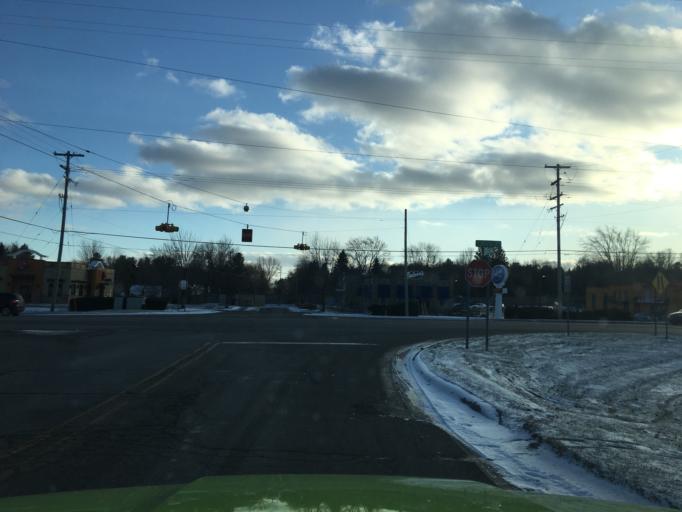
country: US
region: Michigan
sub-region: Montcalm County
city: Greenville
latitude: 43.1775
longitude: -85.2831
